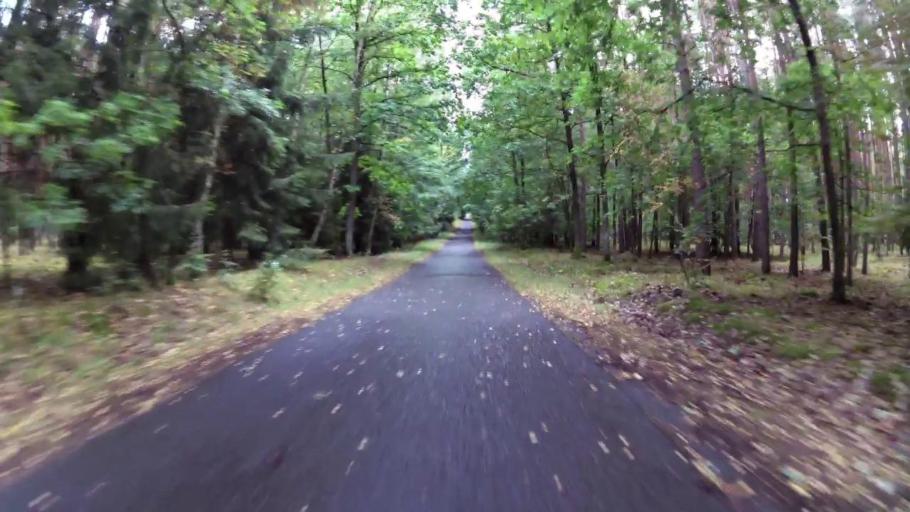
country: PL
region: West Pomeranian Voivodeship
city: Trzcinsko Zdroj
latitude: 52.8931
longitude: 14.7021
